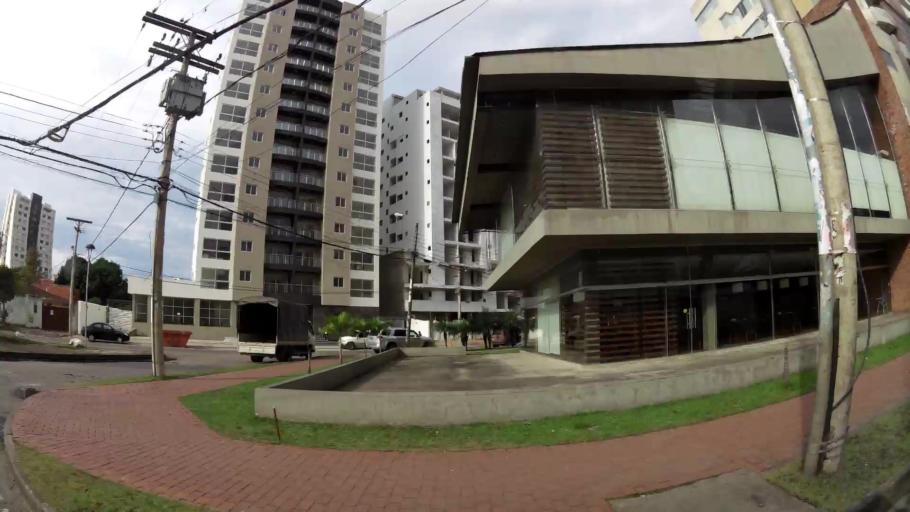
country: BO
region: Santa Cruz
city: Santa Cruz de la Sierra
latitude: -17.7931
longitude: -63.1763
